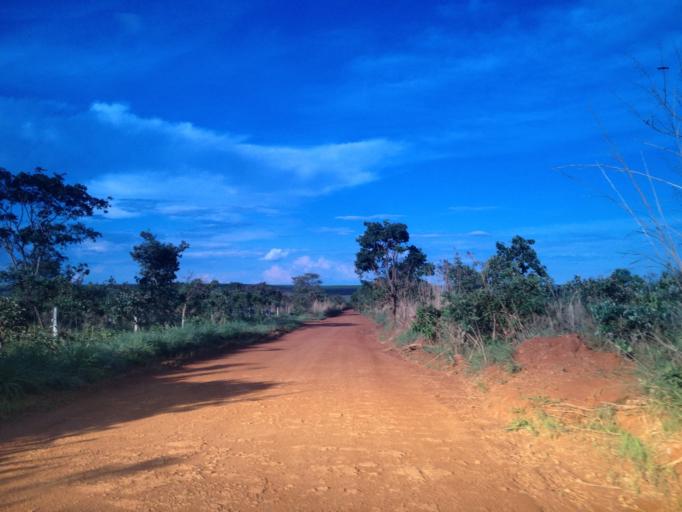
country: BR
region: Goias
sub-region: Abadiania
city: Abadiania
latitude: -16.0026
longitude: -48.5551
